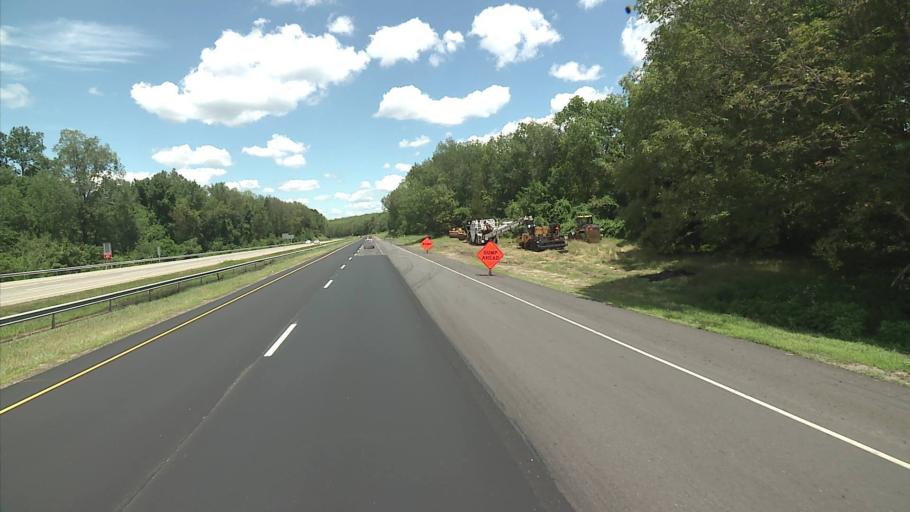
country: US
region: Connecticut
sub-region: Windham County
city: Danielson
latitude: 41.8121
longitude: -71.8711
